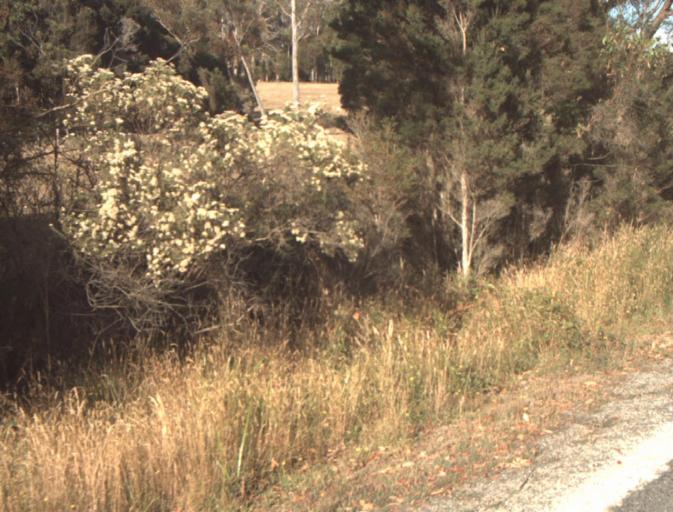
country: AU
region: Tasmania
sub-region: Dorset
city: Bridport
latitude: -41.1623
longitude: 147.2443
